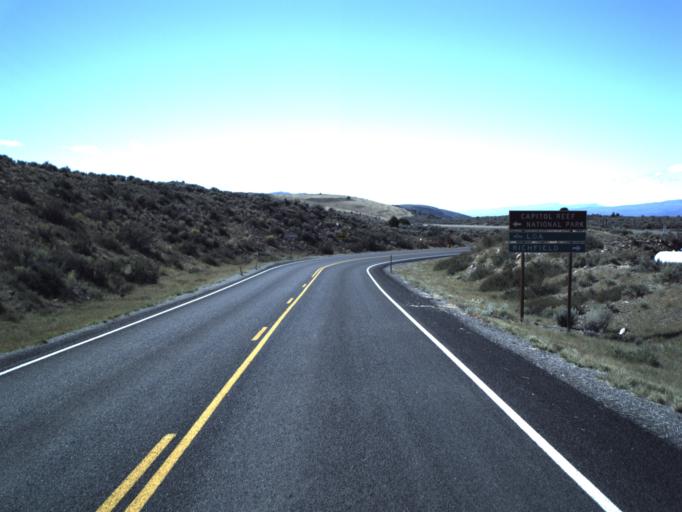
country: US
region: Utah
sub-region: Wayne County
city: Loa
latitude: 38.4734
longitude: -111.8316
